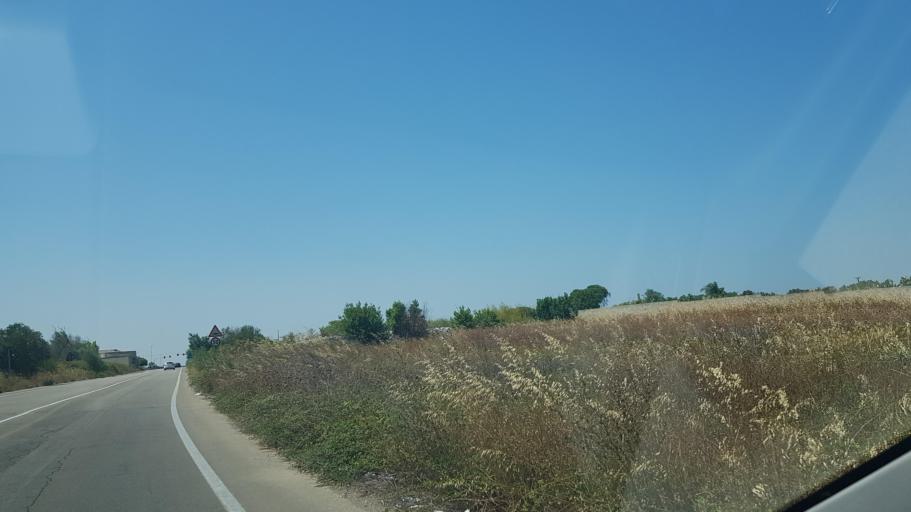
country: IT
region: Apulia
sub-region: Provincia di Lecce
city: Vernole
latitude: 40.2903
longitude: 18.3081
